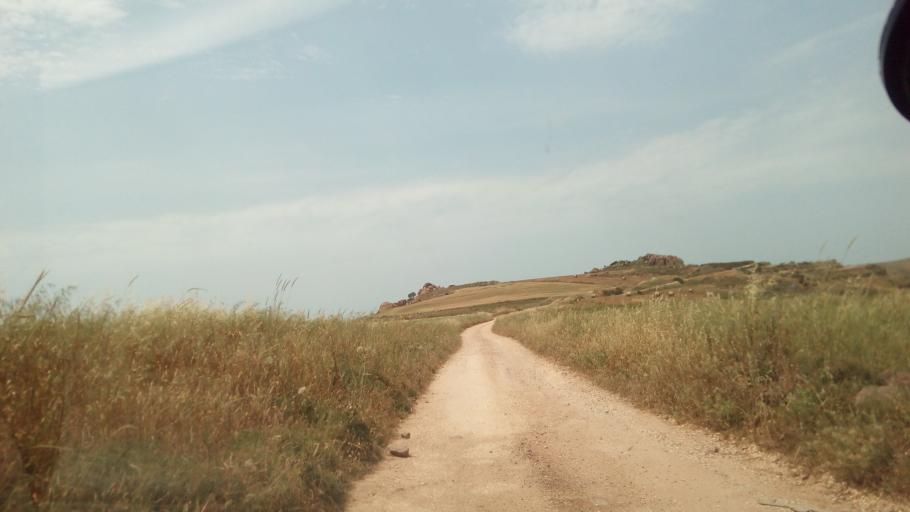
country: CY
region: Pafos
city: Polis
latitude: 34.9796
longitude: 32.3582
